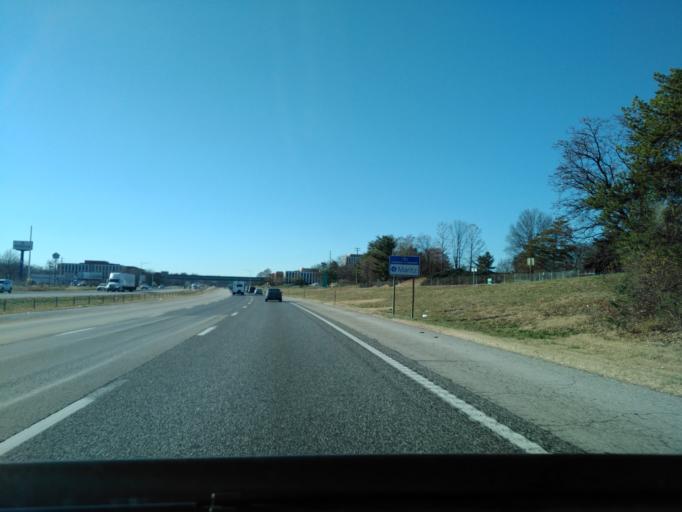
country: US
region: Missouri
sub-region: Saint Louis County
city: Valley Park
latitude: 38.5428
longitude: -90.4705
